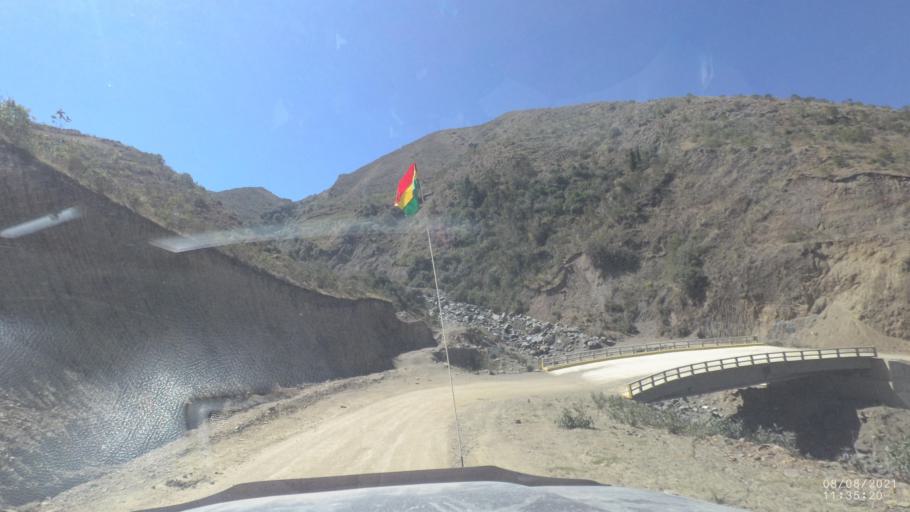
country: BO
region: Cochabamba
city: Colchani
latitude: -16.7773
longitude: -66.6445
